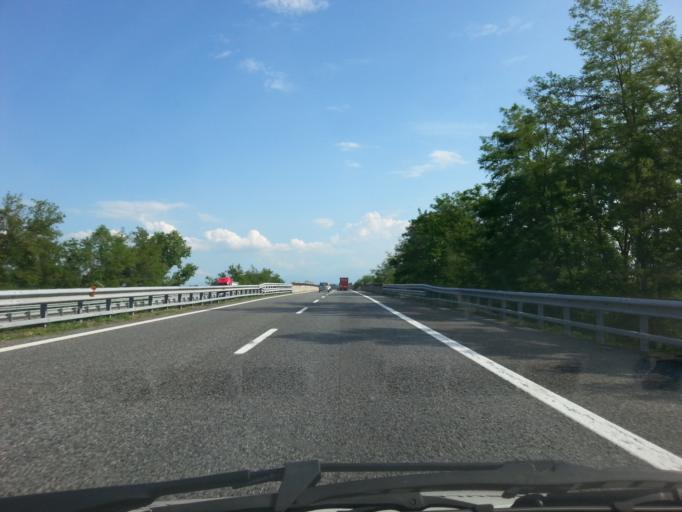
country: IT
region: Piedmont
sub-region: Provincia di Cuneo
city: Marene
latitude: 44.6963
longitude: 7.7653
